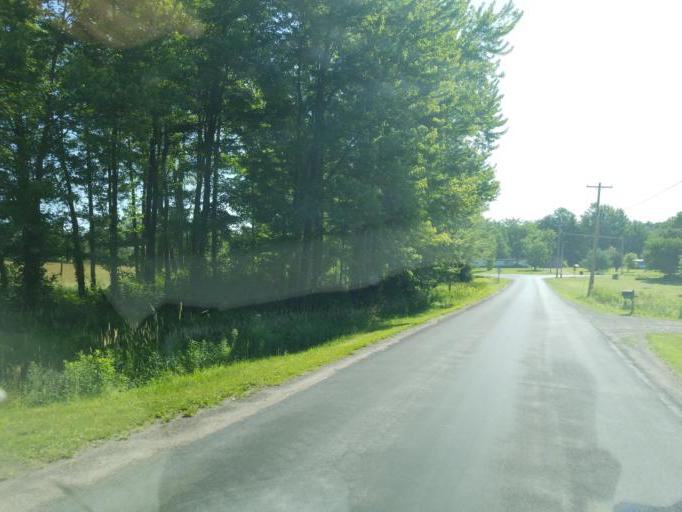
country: US
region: New York
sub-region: Wayne County
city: Clyde
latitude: 43.1136
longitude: -76.8419
